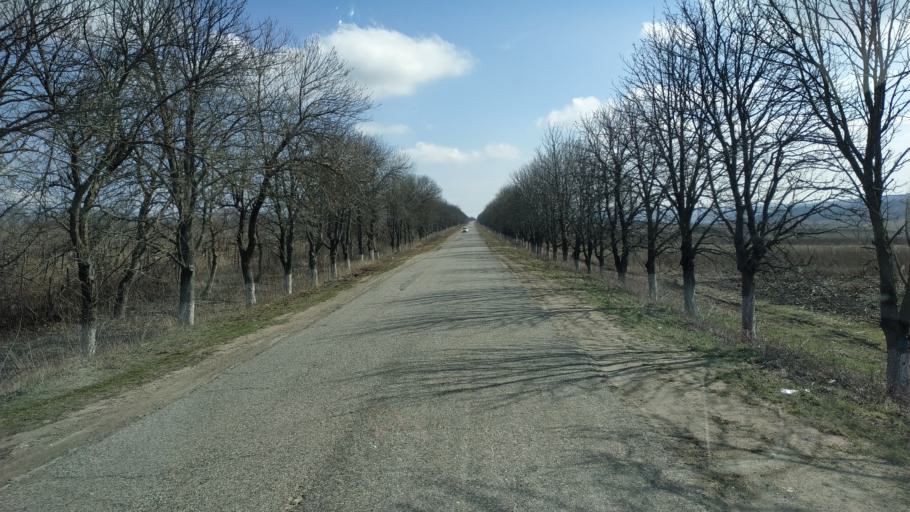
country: MD
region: Hincesti
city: Hincesti
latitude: 46.8565
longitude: 28.6374
